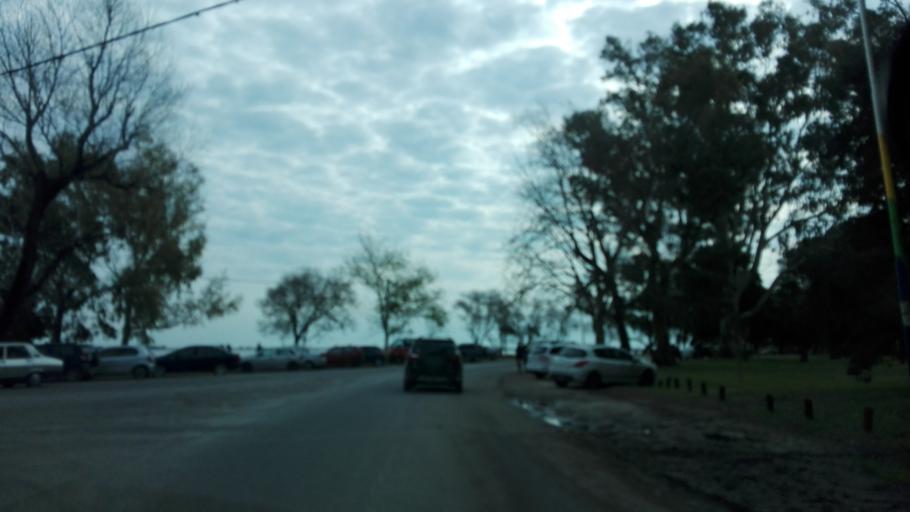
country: AR
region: Buenos Aires
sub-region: Partido de Chascomus
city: Chascomus
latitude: -35.5819
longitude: -58.0180
